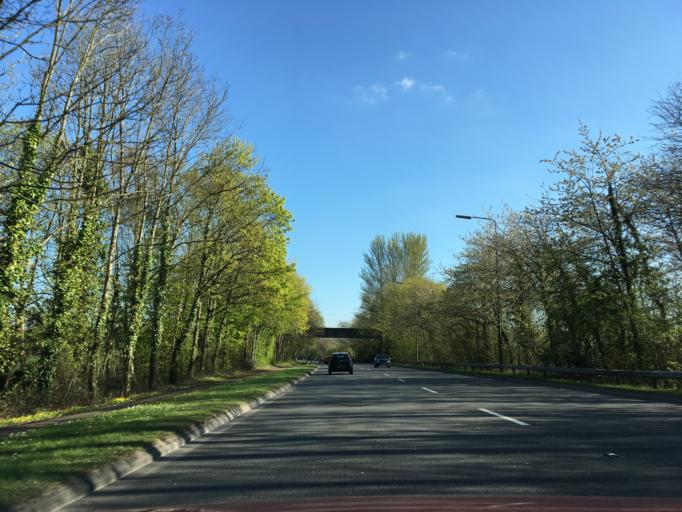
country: GB
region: Wales
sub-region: Torfaen County Borough
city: Cwmbran
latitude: 51.6309
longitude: -3.0191
